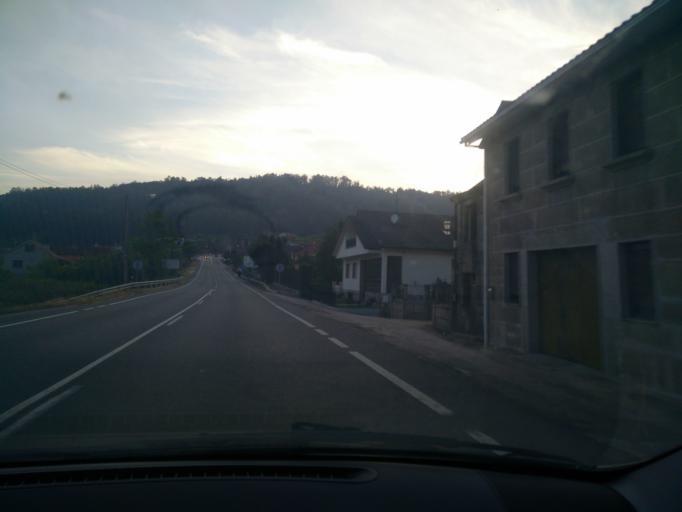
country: ES
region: Galicia
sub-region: Provincia de Pontevedra
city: Porrino
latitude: 42.1799
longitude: -8.5643
